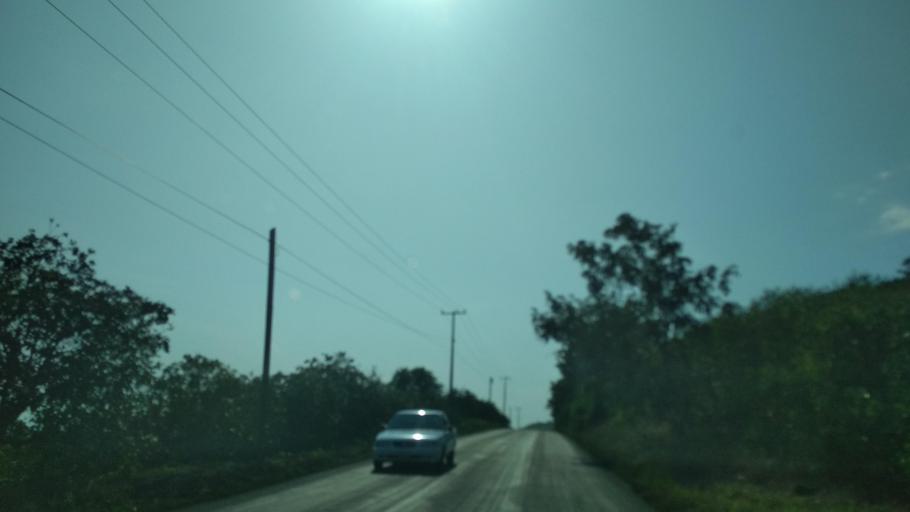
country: MX
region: Veracruz
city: Agua Dulce
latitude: 20.3954
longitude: -97.2718
